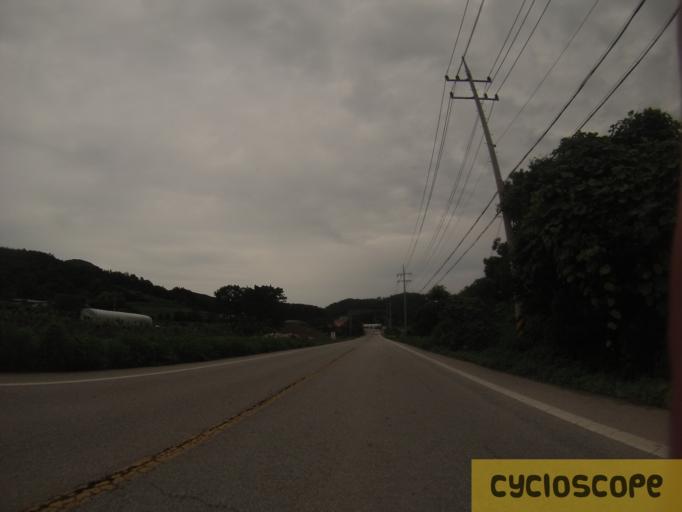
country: KR
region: Jeollabuk-do
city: Puan
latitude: 35.7561
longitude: 126.7614
